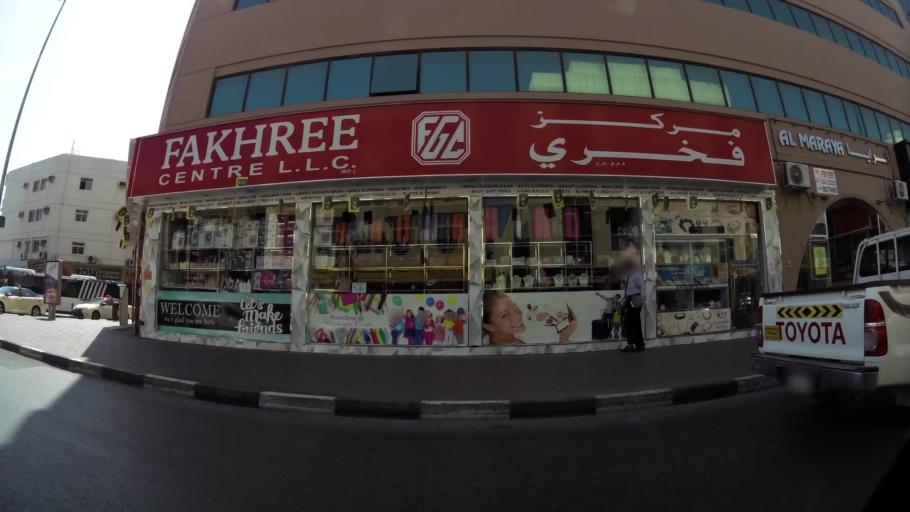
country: AE
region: Ash Shariqah
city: Sharjah
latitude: 25.2340
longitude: 55.2780
